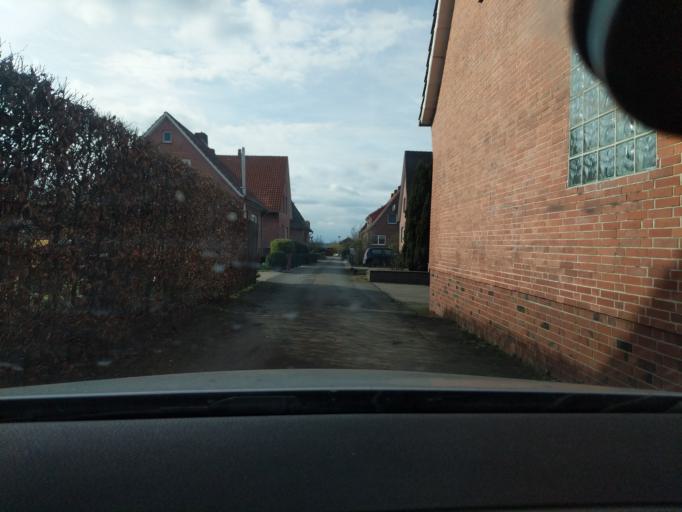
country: DE
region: Lower Saxony
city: Guderhandviertel
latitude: 53.5415
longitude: 9.6116
